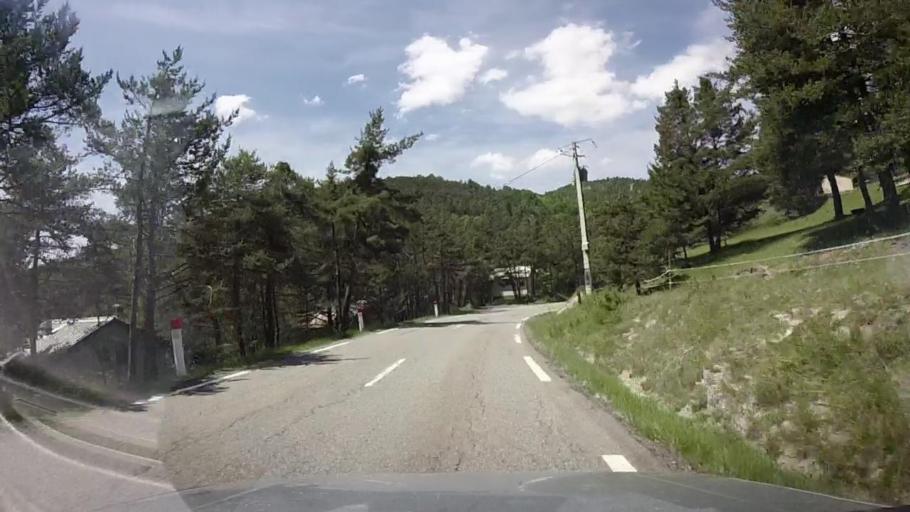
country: FR
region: Provence-Alpes-Cote d'Azur
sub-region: Departement des Alpes-de-Haute-Provence
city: Seyne-les-Alpes
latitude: 44.4041
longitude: 6.3339
